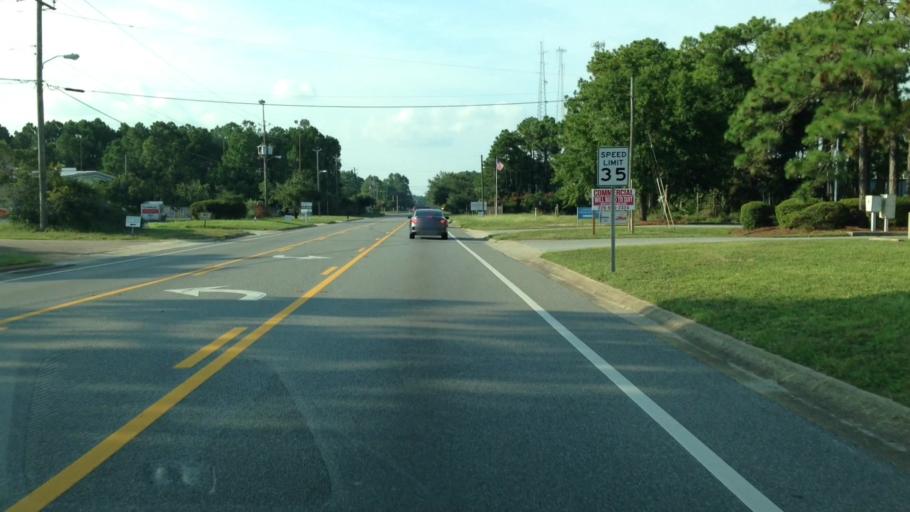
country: US
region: Florida
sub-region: Okaloosa County
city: Mary Esther
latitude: 30.4193
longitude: -86.6673
